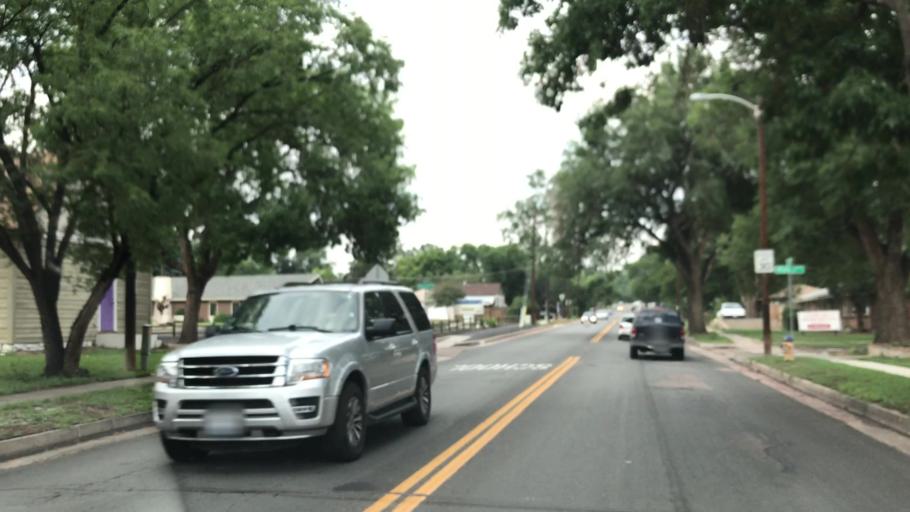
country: US
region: Colorado
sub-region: El Paso County
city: Manitou Springs
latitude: 38.8535
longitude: -104.8684
